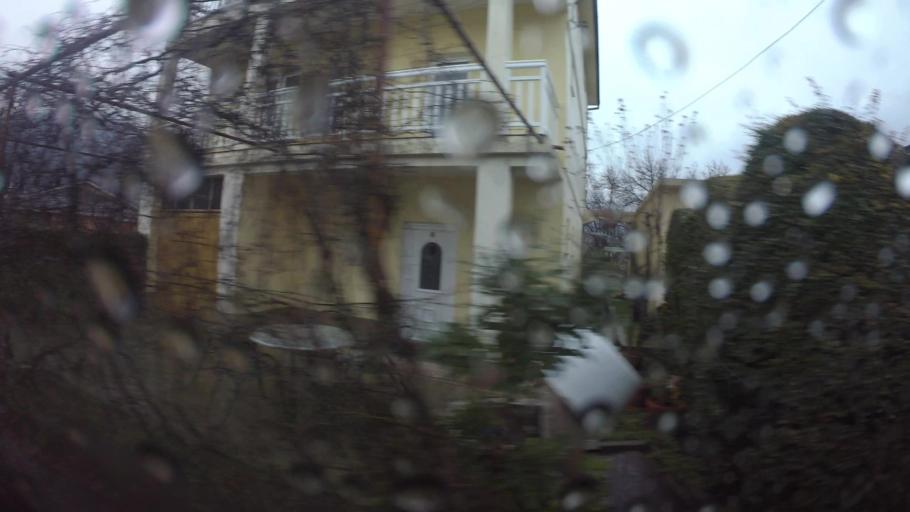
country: BA
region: Federation of Bosnia and Herzegovina
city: Cim
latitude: 43.3469
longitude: 17.7847
